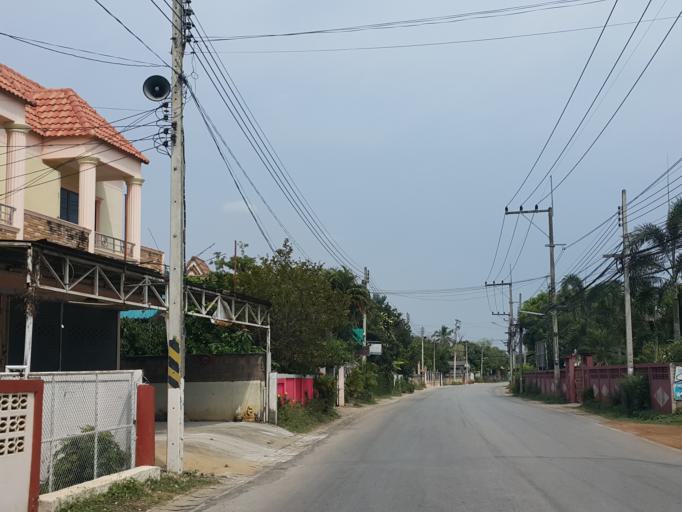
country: TH
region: Lampang
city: Ko Kha
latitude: 18.1833
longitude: 99.3942
